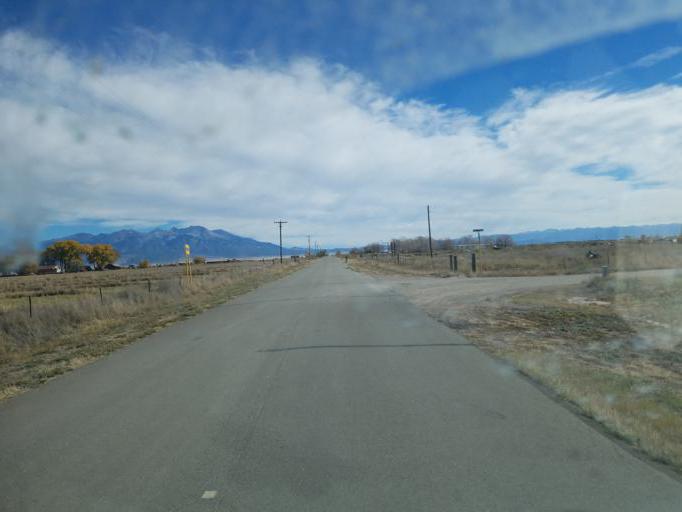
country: US
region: Colorado
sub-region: Alamosa County
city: Alamosa East
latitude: 37.5037
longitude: -105.8039
